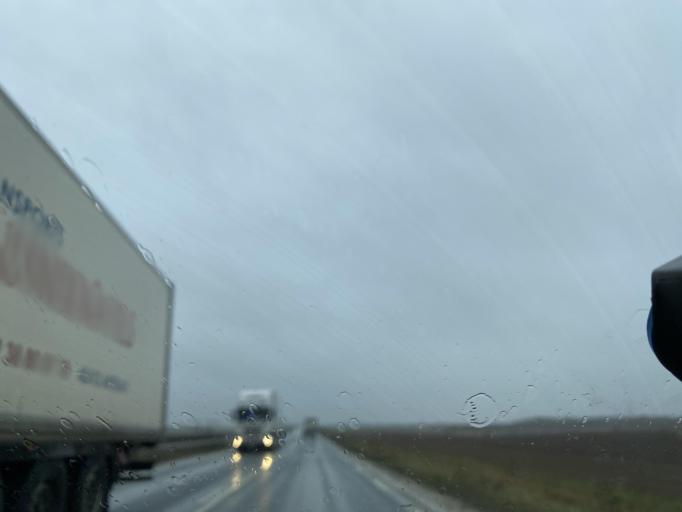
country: FR
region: Centre
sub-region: Departement d'Eure-et-Loir
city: Voves
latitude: 48.2904
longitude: 1.7144
